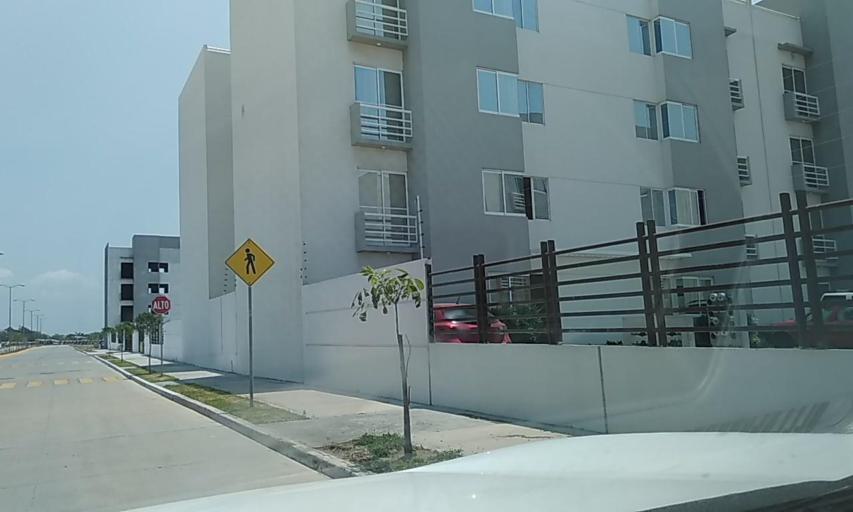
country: MX
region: Veracruz
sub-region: Veracruz
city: Hacienda Sotavento
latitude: 19.1245
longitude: -96.1713
